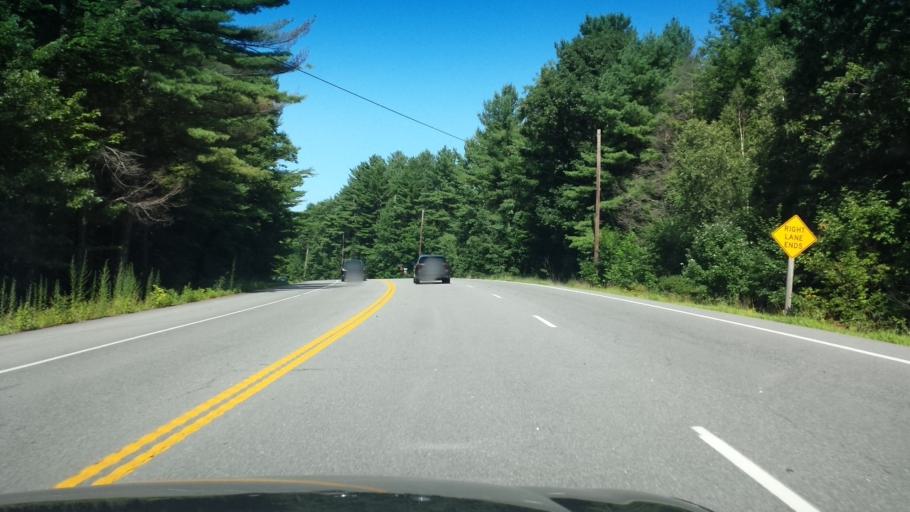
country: US
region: Maine
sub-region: York County
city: Sanford (historical)
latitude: 43.4302
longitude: -70.8012
